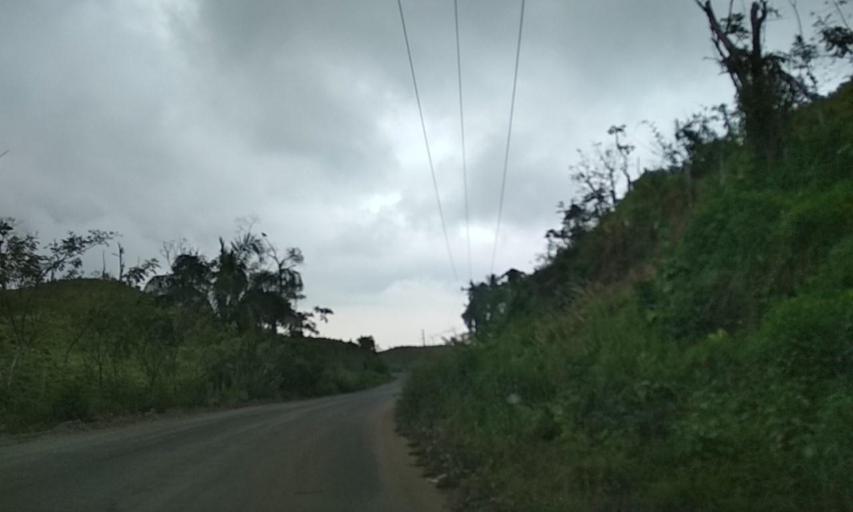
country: MX
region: Tabasco
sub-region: Huimanguillo
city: Francisco Rueda
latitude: 17.6404
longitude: -94.0930
